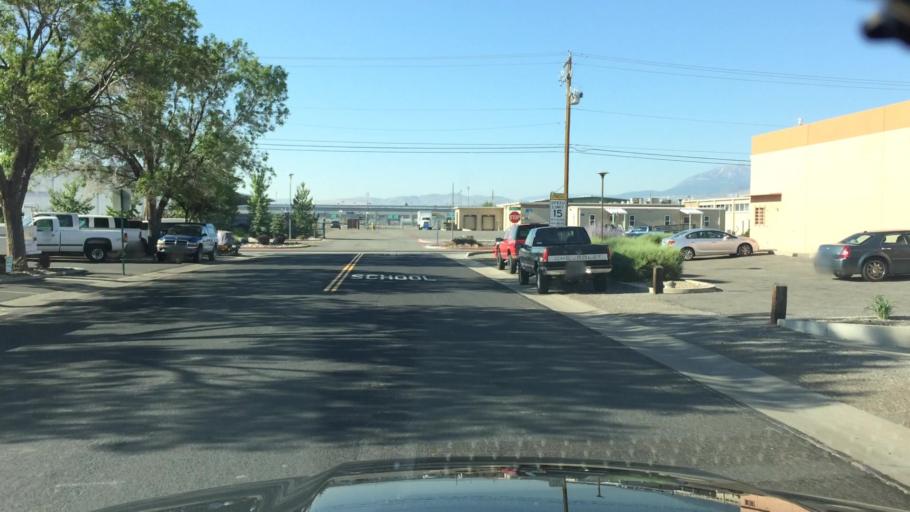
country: US
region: Nevada
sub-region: Washoe County
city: Sparks
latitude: 39.5137
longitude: -119.7754
